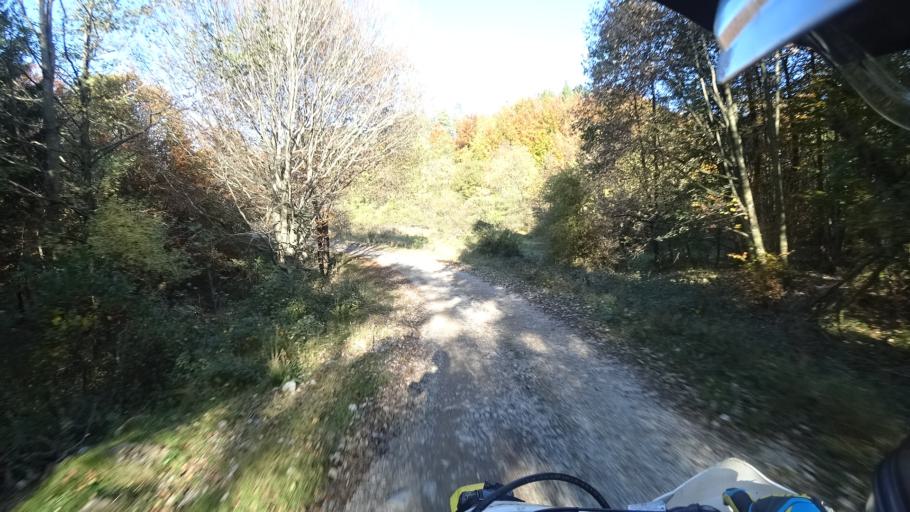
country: HR
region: Primorsko-Goranska
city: Klana
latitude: 45.4796
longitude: 14.3623
